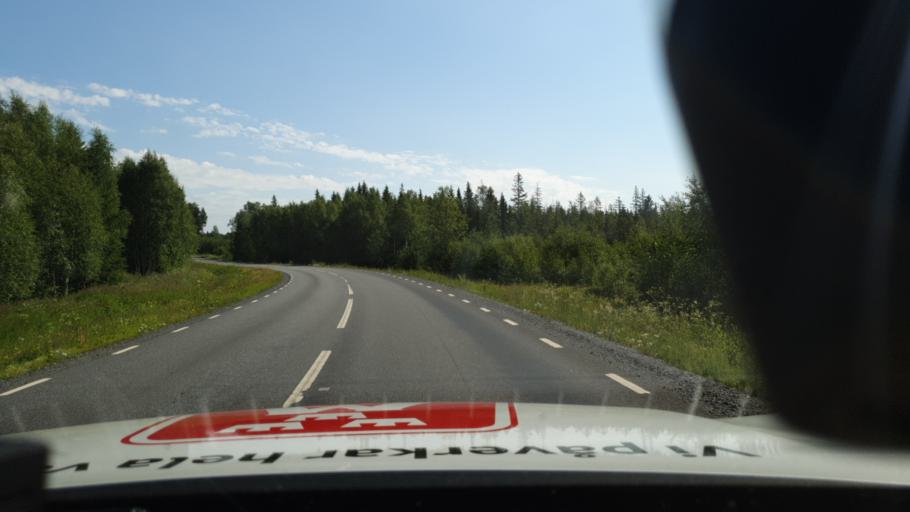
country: SE
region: Norrbotten
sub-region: Lulea Kommun
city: Gammelstad
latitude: 65.7868
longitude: 22.1040
